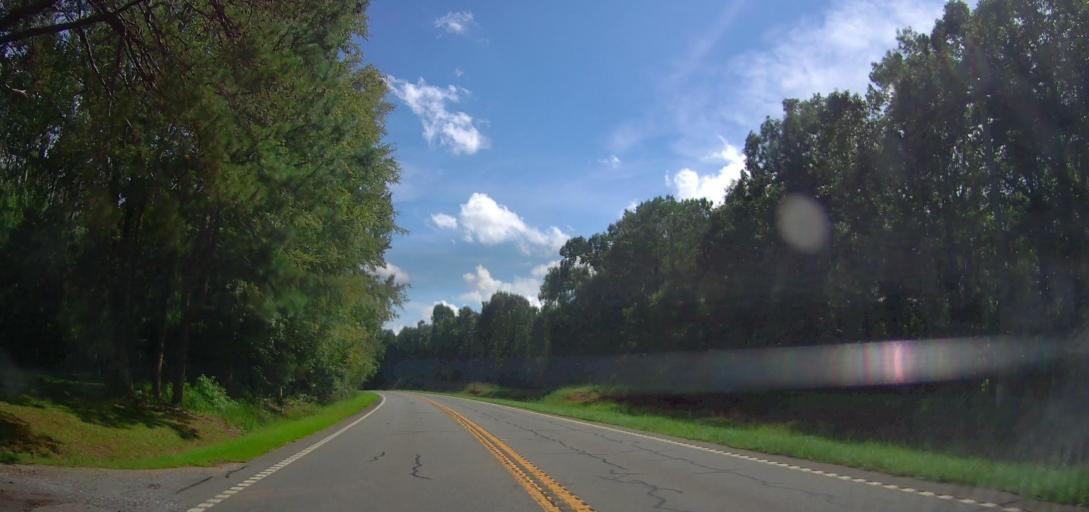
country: US
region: Georgia
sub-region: Talbot County
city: Talbotton
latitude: 32.7582
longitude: -84.5577
